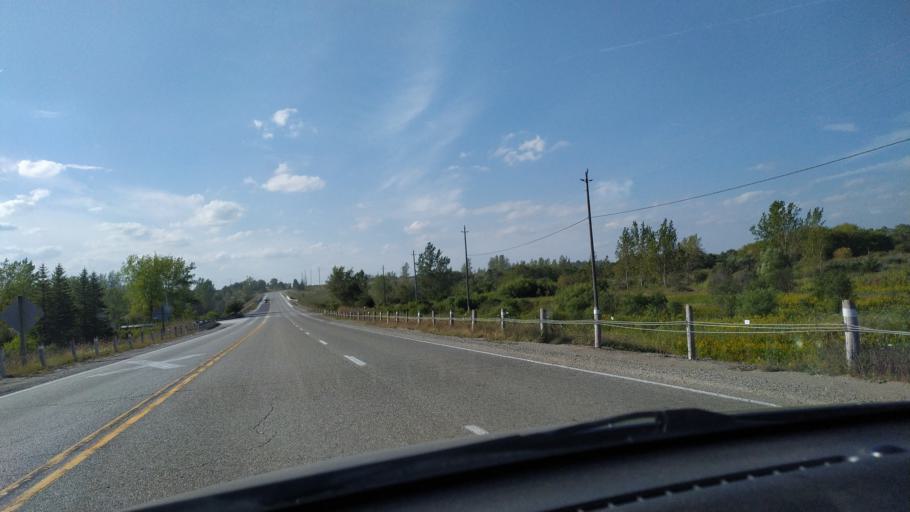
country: CA
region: Ontario
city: Ingersoll
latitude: 43.0700
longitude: -80.8506
